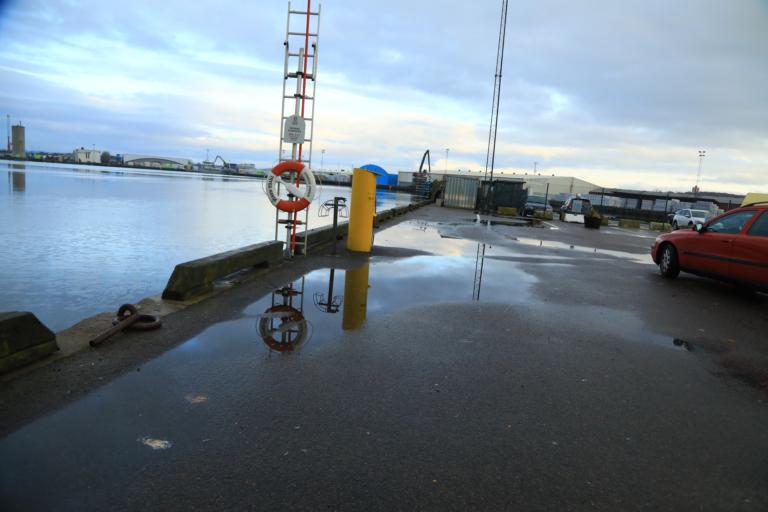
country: SE
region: Halland
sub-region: Varbergs Kommun
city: Varberg
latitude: 57.1101
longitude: 12.2421
